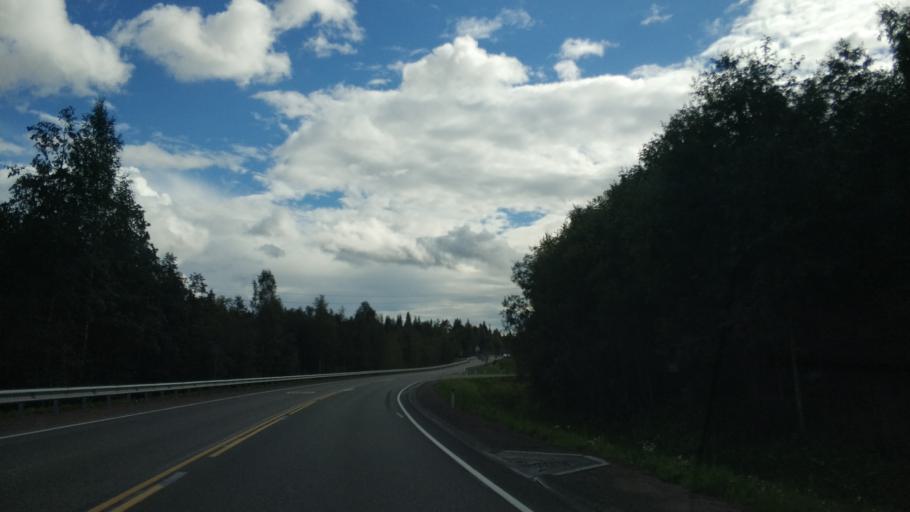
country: RU
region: Republic of Karelia
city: Khelyulya
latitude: 61.7836
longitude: 30.6555
